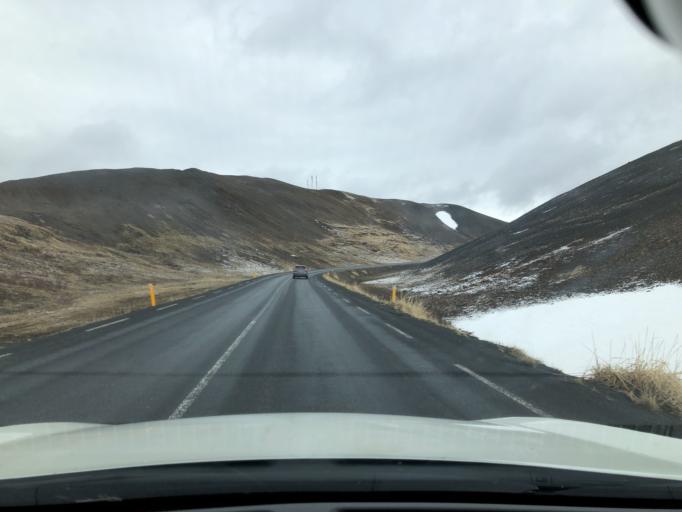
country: IS
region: Northeast
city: Laugar
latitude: 65.6451
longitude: -16.8302
